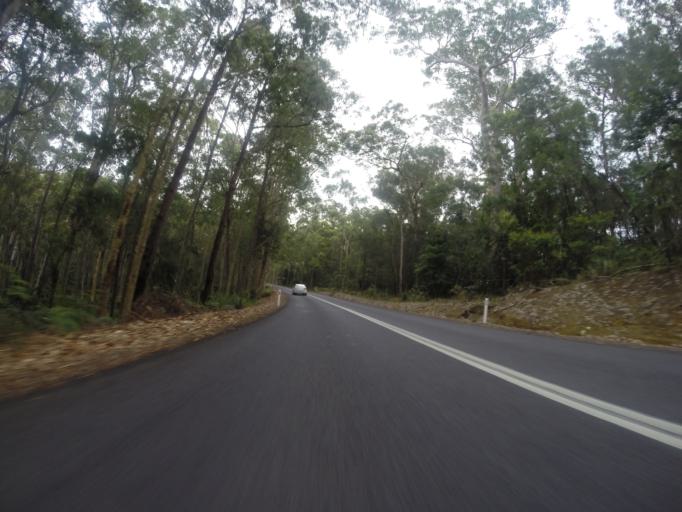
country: AU
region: New South Wales
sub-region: Eurobodalla
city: Batemans Bay
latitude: -35.6570
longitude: 150.2907
